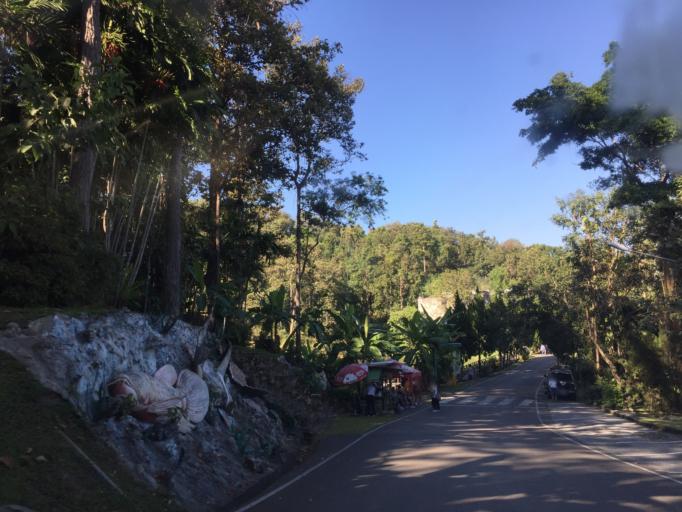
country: TH
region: Chiang Mai
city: Chiang Mai
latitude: 18.8079
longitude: 98.9418
